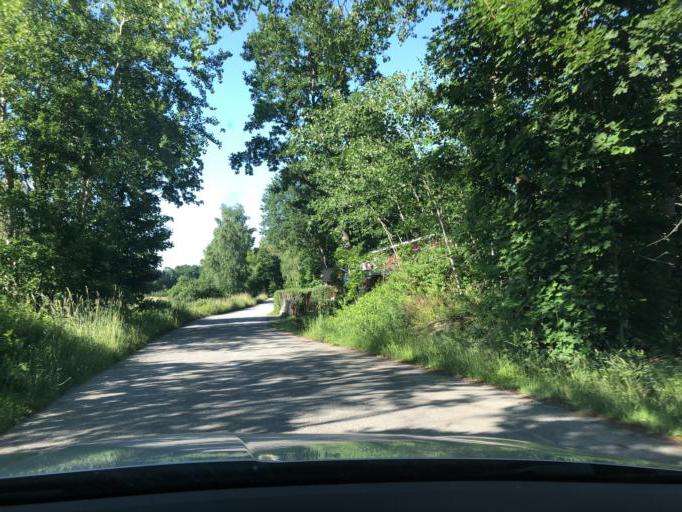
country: SE
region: Blekinge
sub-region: Karlshamns Kommun
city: Morrum
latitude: 56.1620
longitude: 14.8016
